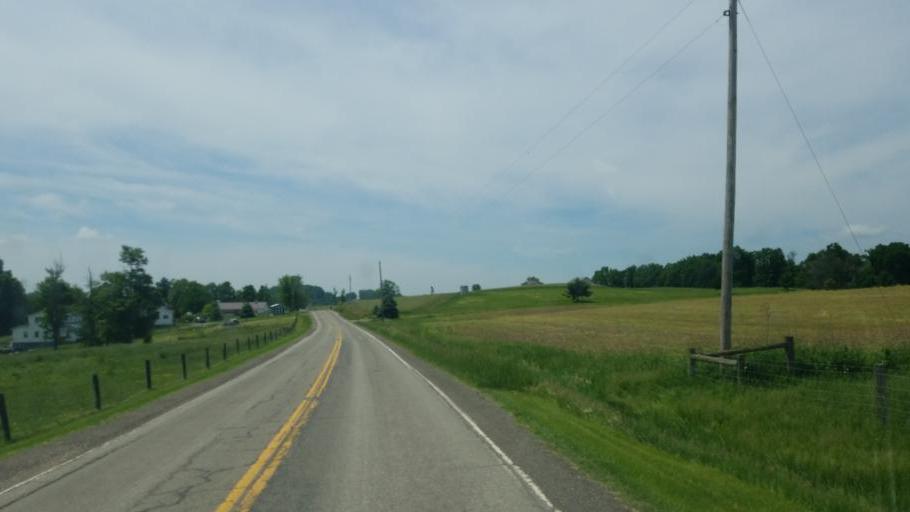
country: US
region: Ohio
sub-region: Tuscarawas County
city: Sugarcreek
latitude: 40.4357
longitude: -81.7823
